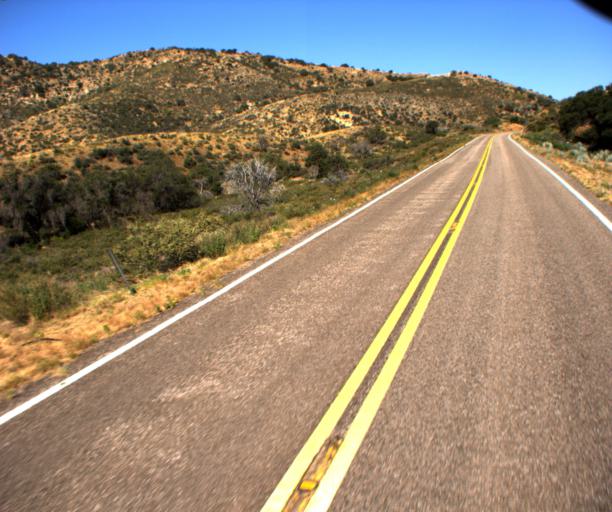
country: US
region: Arizona
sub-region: Graham County
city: Swift Trail Junction
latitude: 32.5747
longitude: -109.8364
